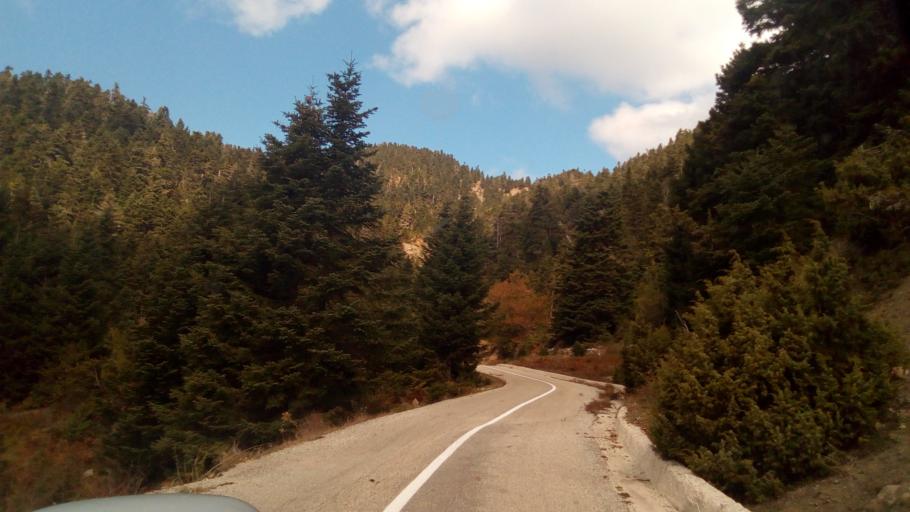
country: GR
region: West Greece
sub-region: Nomos Aitolias kai Akarnanias
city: Nafpaktos
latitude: 38.6385
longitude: 21.9347
